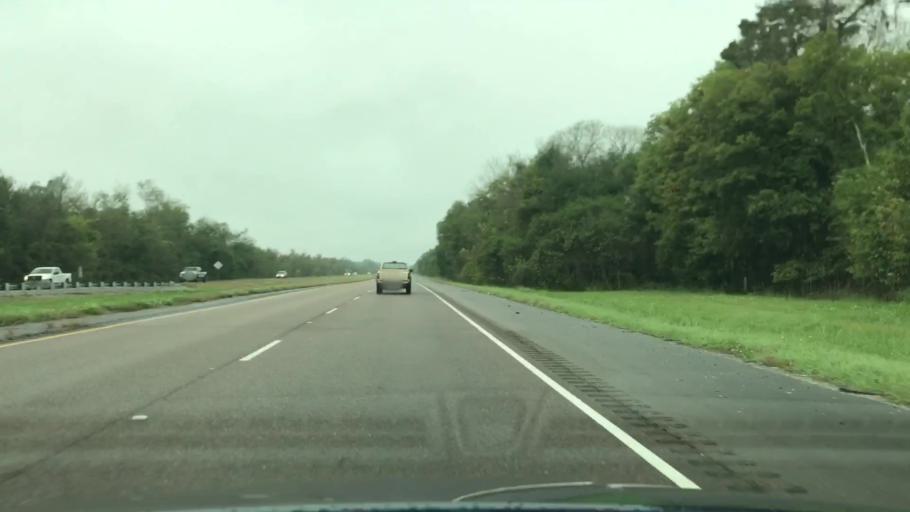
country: US
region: Louisiana
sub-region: Terrebonne Parish
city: Bayou Cane
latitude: 29.6870
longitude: -90.7042
